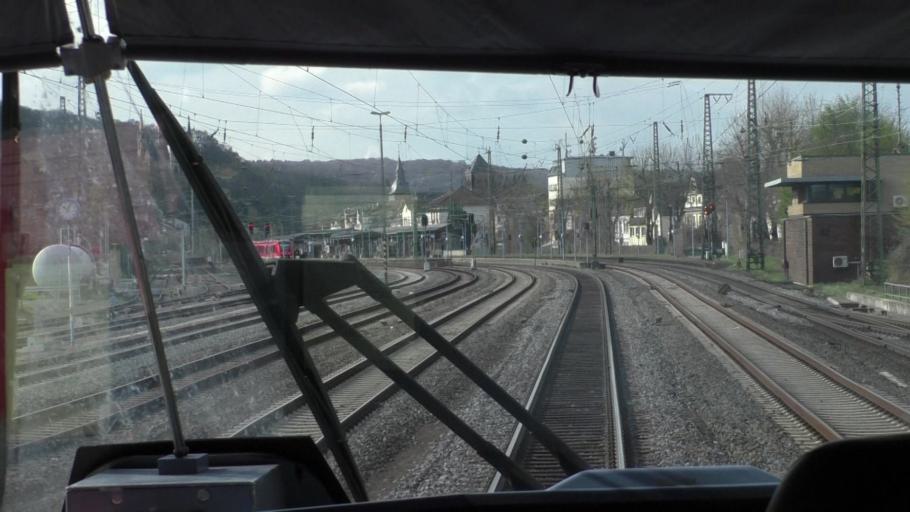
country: DE
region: Rheinland-Pfalz
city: Erpel
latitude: 50.5744
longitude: 7.2352
